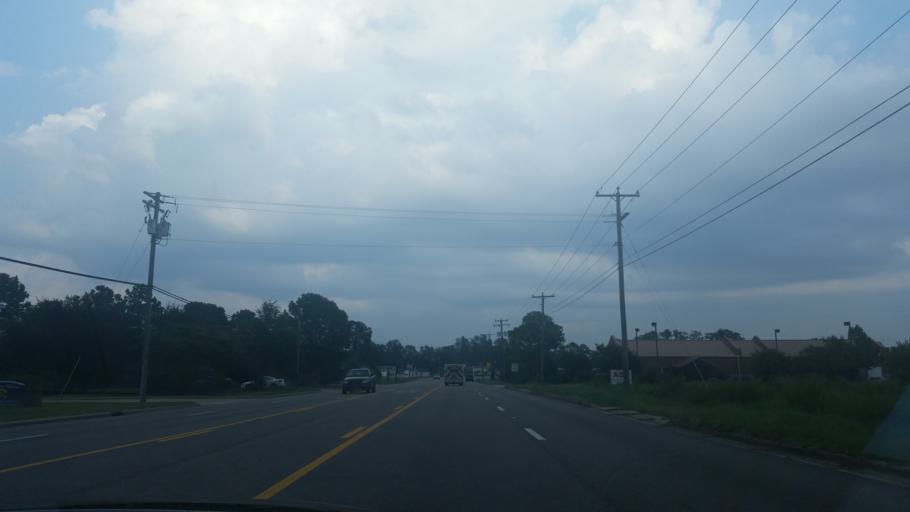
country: US
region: North Carolina
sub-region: Dare County
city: Southern Shores
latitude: 36.2439
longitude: -75.8823
